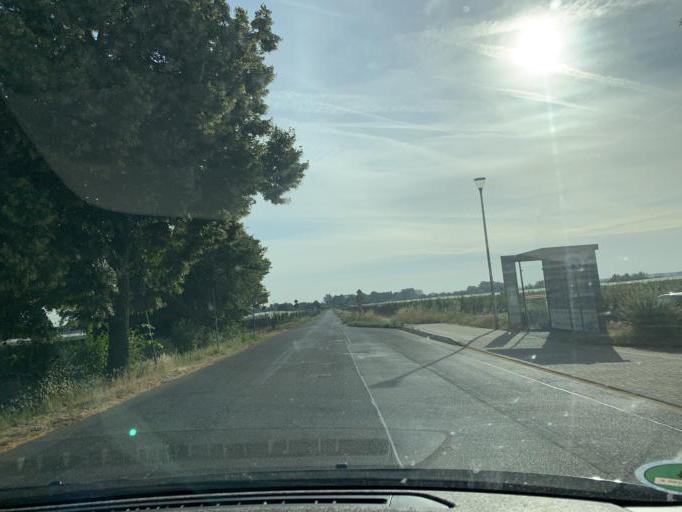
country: DE
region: North Rhine-Westphalia
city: Bruhl
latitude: 50.7804
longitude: 6.9332
